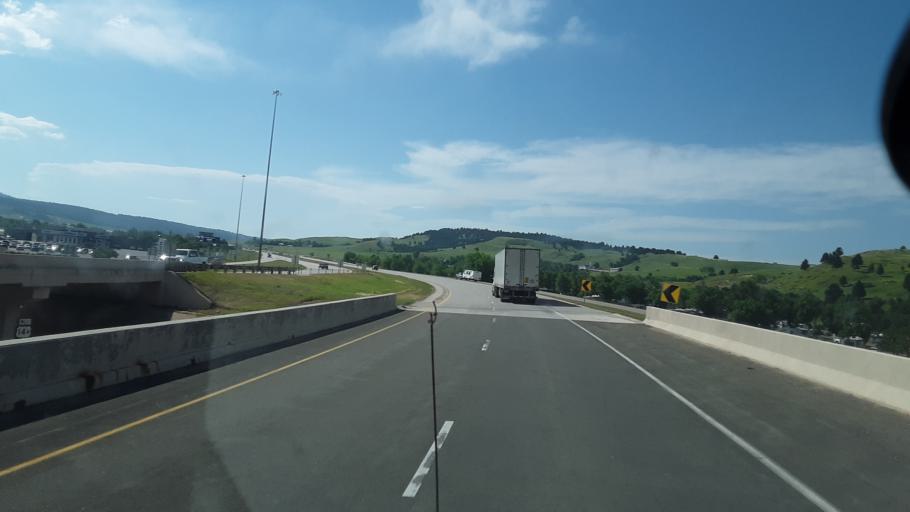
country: US
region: South Dakota
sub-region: Meade County
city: Sturgis
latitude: 44.4187
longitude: -103.5320
